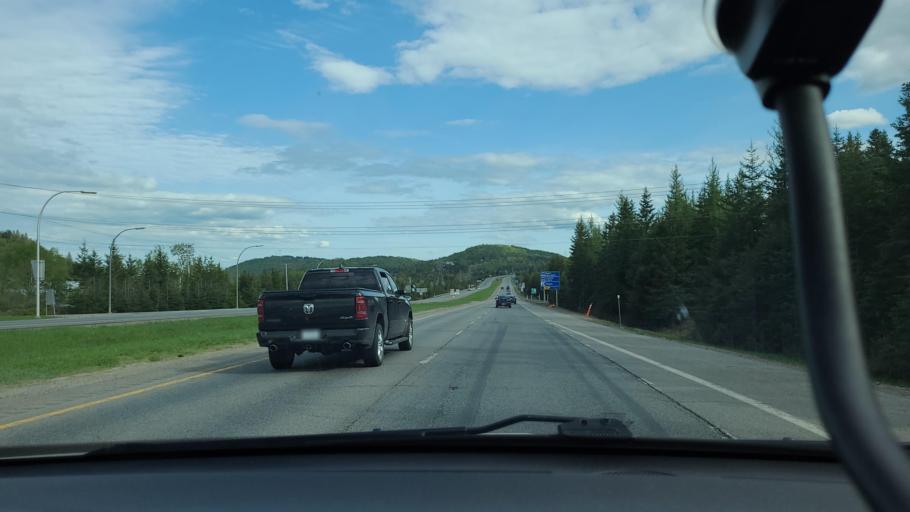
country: CA
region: Quebec
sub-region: Laurentides
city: Sainte-Agathe-des-Monts
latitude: 46.0574
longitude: -74.2736
